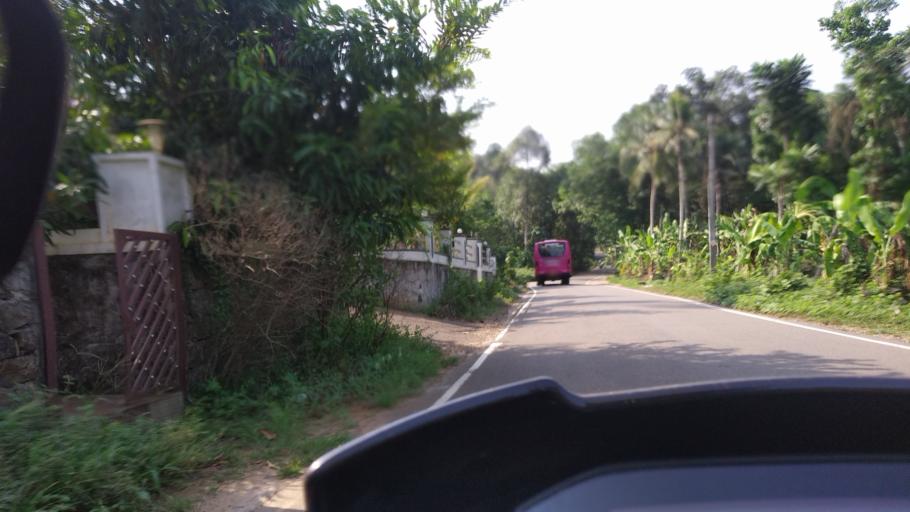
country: IN
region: Kerala
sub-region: Ernakulam
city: Piravam
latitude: 9.8151
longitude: 76.5597
